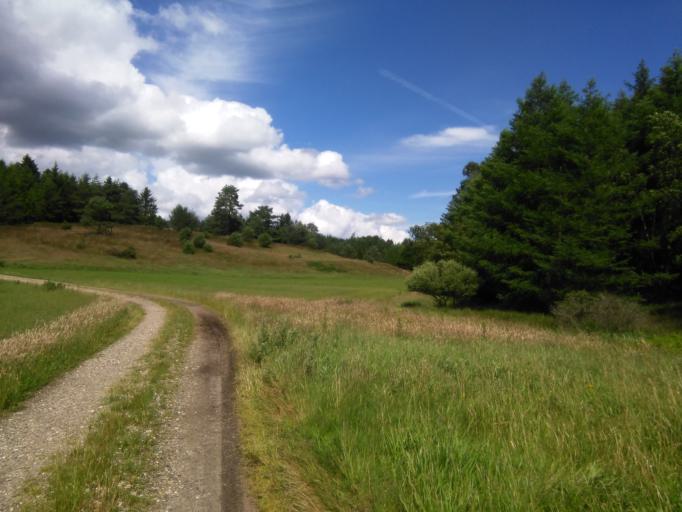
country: DK
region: Central Jutland
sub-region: Silkeborg Kommune
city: Virklund
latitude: 56.0808
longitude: 9.4415
